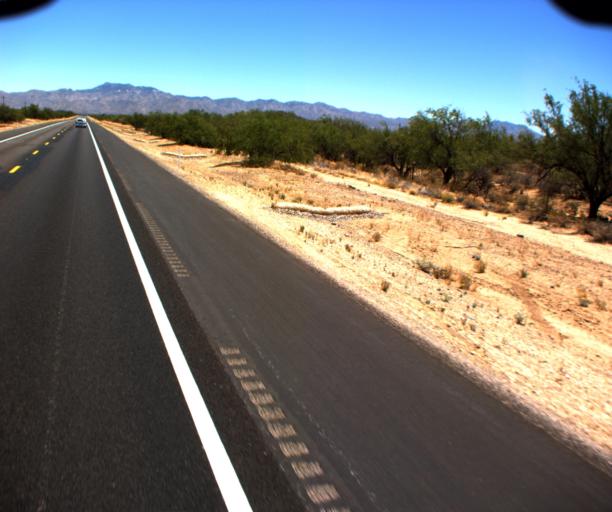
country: US
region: Arizona
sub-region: Pima County
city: Sells
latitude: 31.9218
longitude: -111.8197
